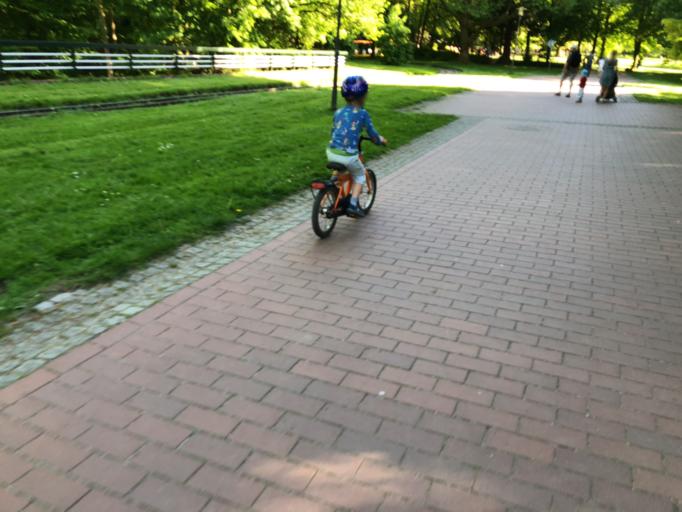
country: DE
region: North Rhine-Westphalia
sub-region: Regierungsbezirk Dusseldorf
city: Essen
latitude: 51.4280
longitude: 6.9836
